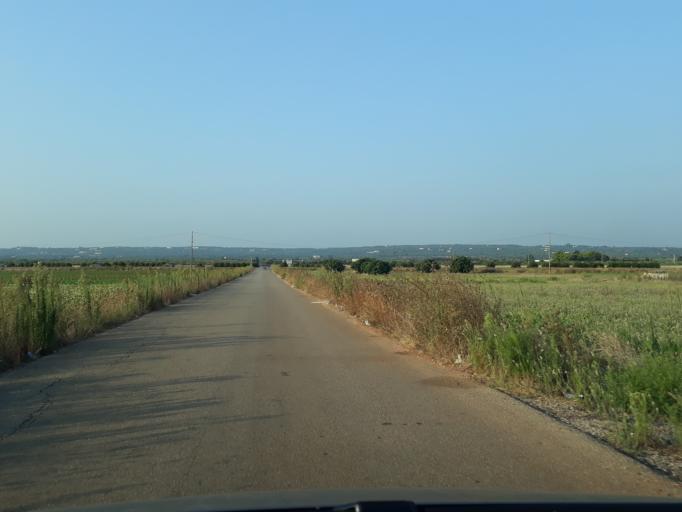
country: IT
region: Apulia
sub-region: Provincia di Brindisi
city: Carovigno
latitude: 40.7498
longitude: 17.7075
